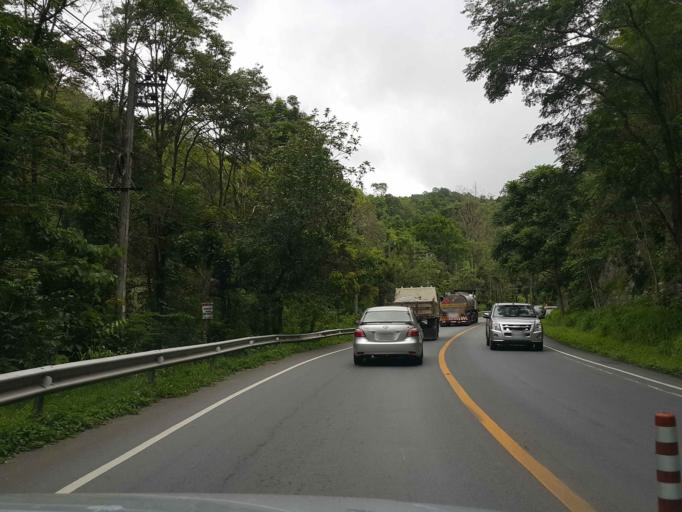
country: TH
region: Tak
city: Tak
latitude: 16.8029
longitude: 98.9563
